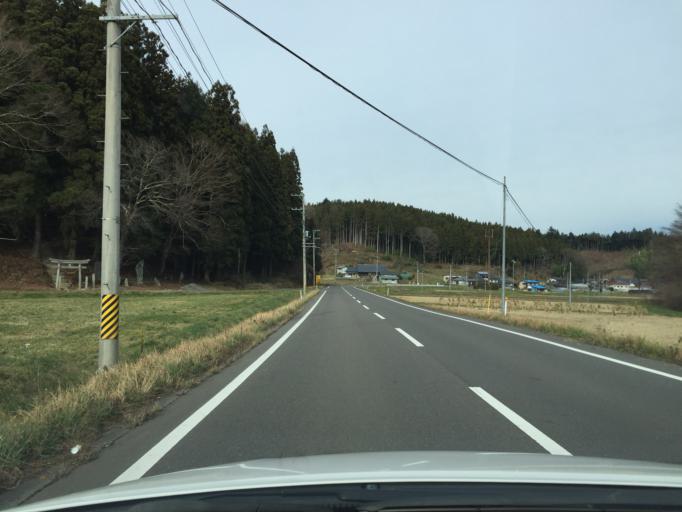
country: JP
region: Fukushima
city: Ishikawa
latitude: 37.2126
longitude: 140.6261
